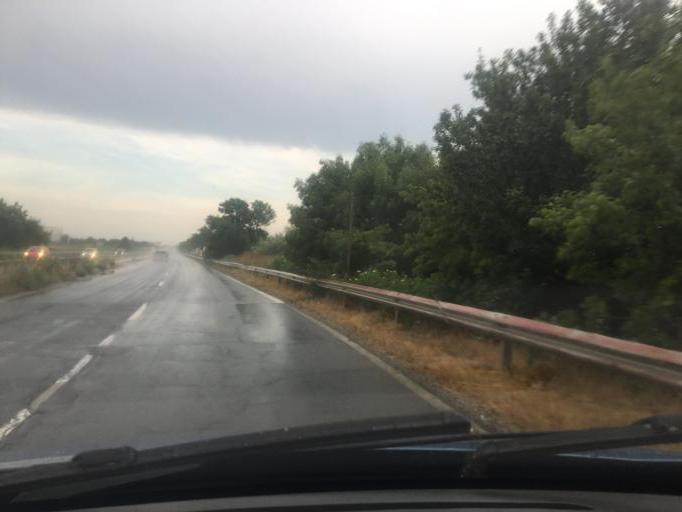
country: BG
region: Burgas
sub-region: Obshtina Burgas
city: Burgas
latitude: 42.5627
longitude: 27.5380
